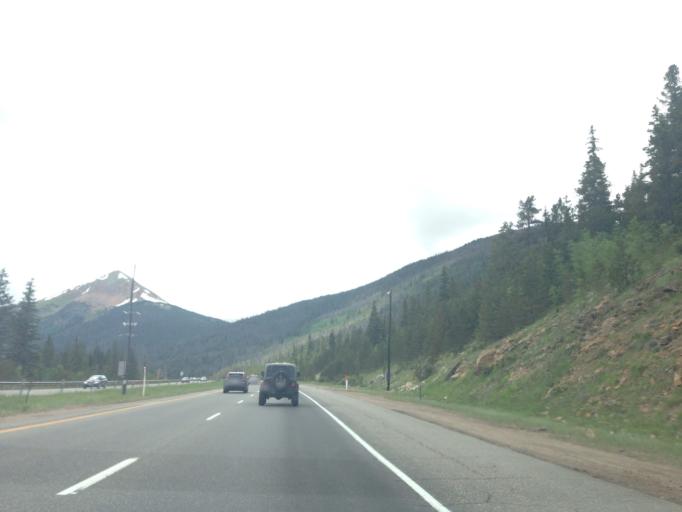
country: US
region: Colorado
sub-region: Clear Creek County
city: Georgetown
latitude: 39.6982
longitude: -105.8321
